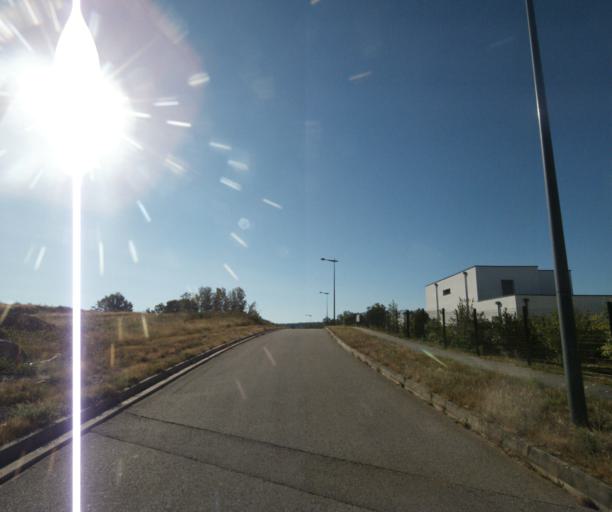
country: FR
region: Lorraine
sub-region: Departement des Vosges
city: Epinal
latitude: 48.1693
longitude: 6.4588
